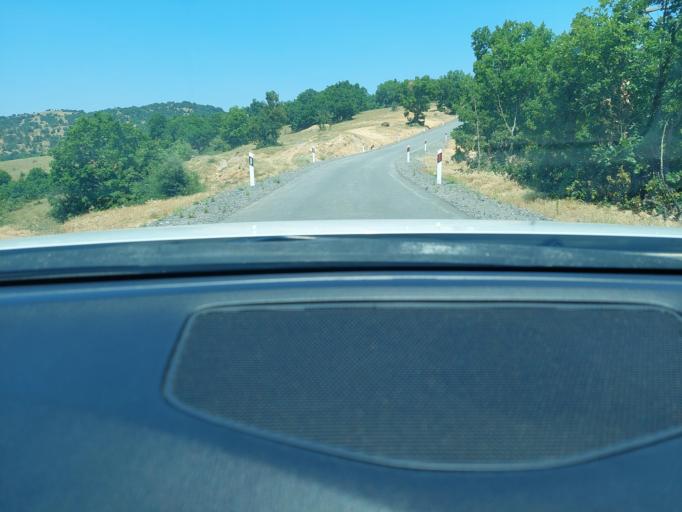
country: MK
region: Radovis
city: Radovish
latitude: 41.6639
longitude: 22.4087
